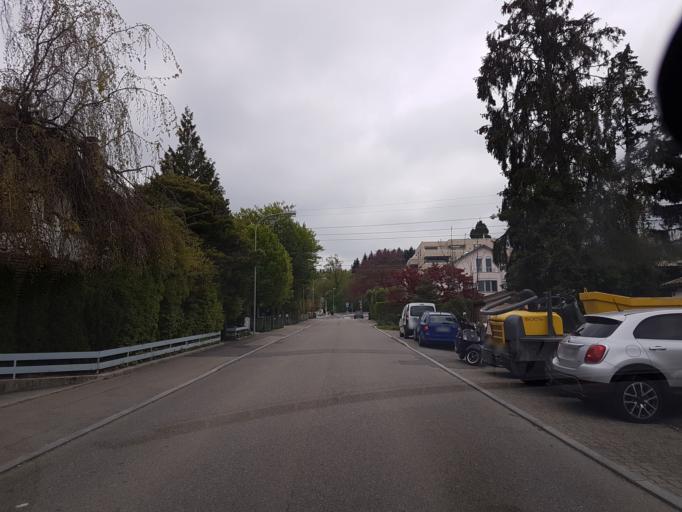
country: CH
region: Zurich
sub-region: Bezirk Dietikon
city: Uitikon
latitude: 47.3687
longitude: 8.4604
